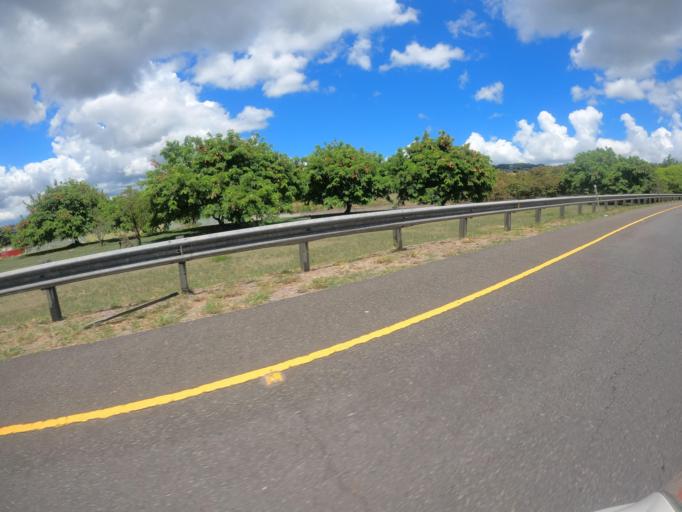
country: US
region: Hawaii
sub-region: Honolulu County
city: Halawa
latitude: 21.3706
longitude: -157.9245
